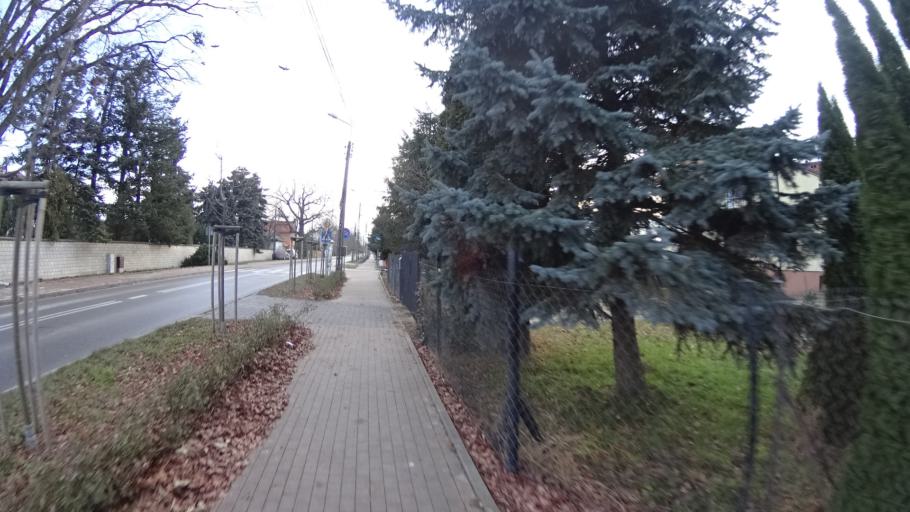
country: PL
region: Masovian Voivodeship
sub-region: Powiat warszawski zachodni
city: Ozarow Mazowiecki
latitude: 52.2254
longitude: 20.8017
